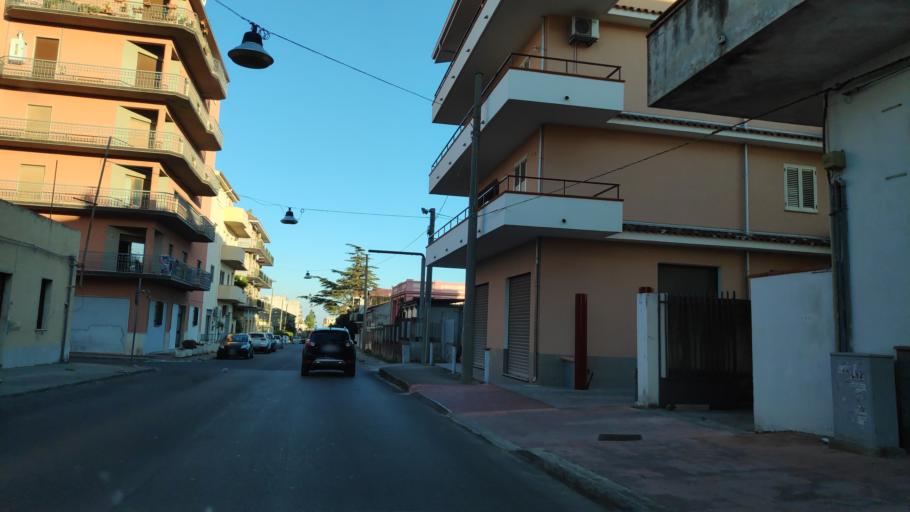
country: IT
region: Calabria
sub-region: Provincia di Reggio Calabria
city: Locri
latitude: 38.2385
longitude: 16.2559
